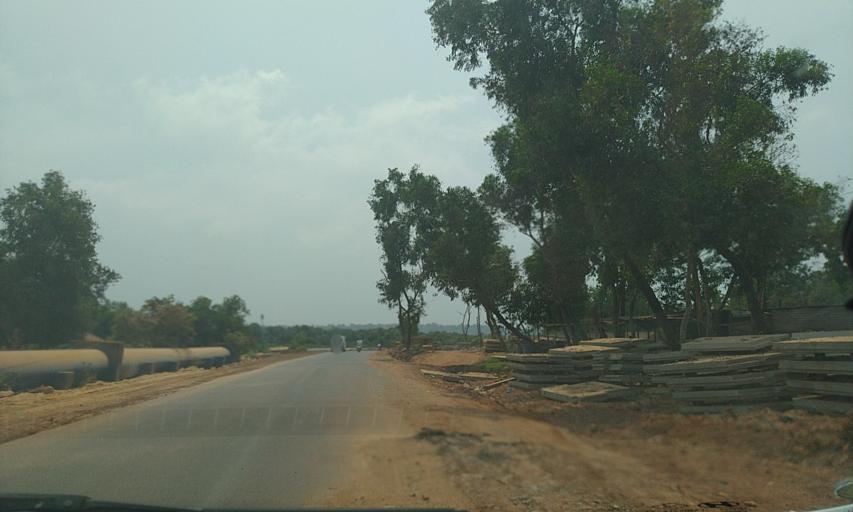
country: IN
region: Goa
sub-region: North Goa
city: Mapuca
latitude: 15.5946
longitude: 73.8253
